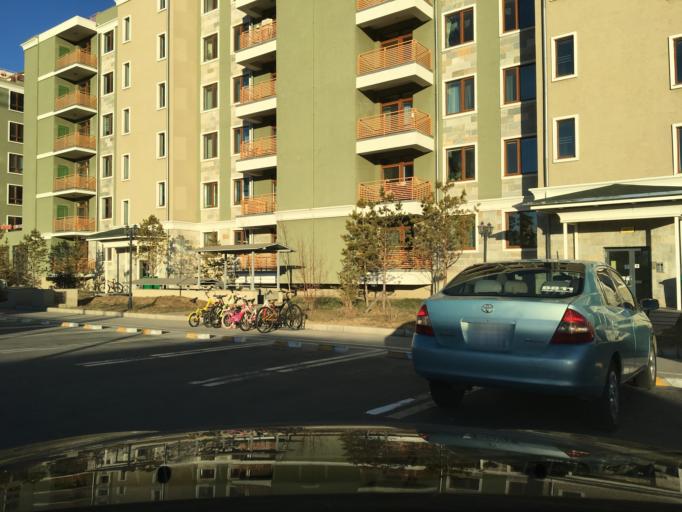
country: MN
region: Ulaanbaatar
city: Ulaanbaatar
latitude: 47.8889
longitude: 106.9286
